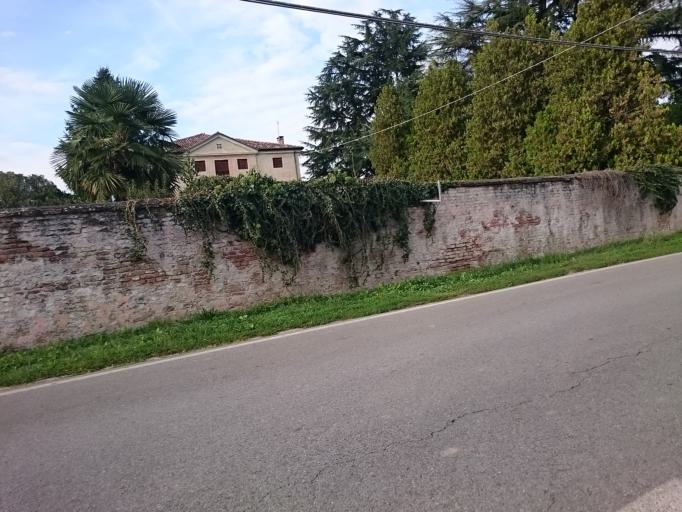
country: IT
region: Veneto
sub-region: Provincia di Vicenza
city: Grumolo delle Abbadesse
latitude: 45.5471
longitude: 11.6699
